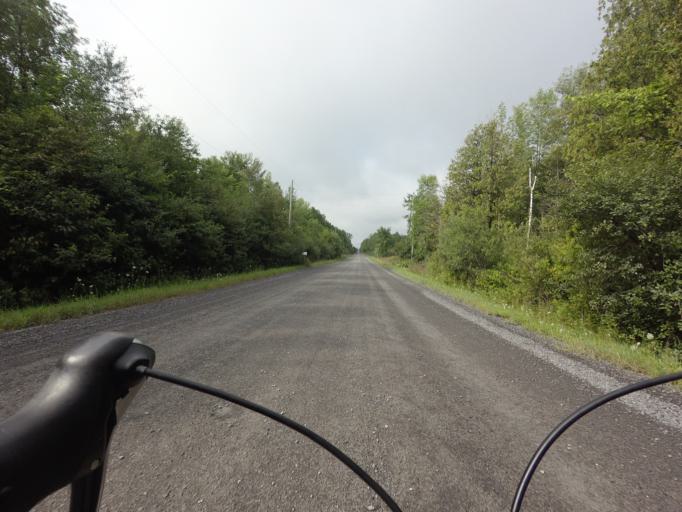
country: CA
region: Ontario
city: Bells Corners
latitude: 45.0514
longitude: -75.7239
